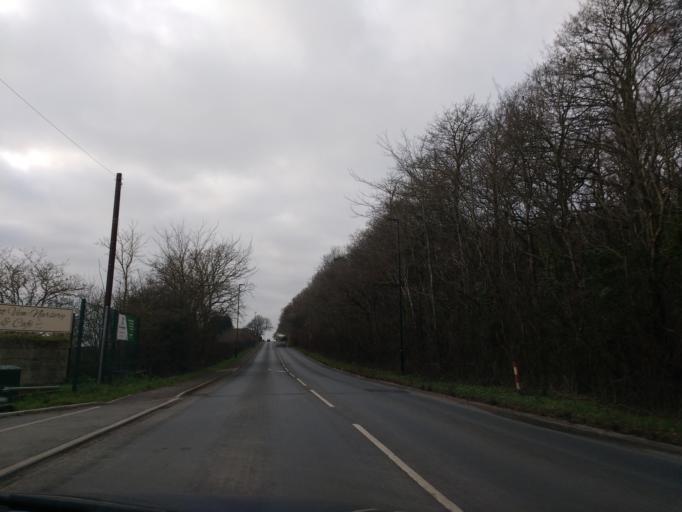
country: GB
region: England
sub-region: Isle of Wight
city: Newport
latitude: 50.7066
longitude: -1.3158
